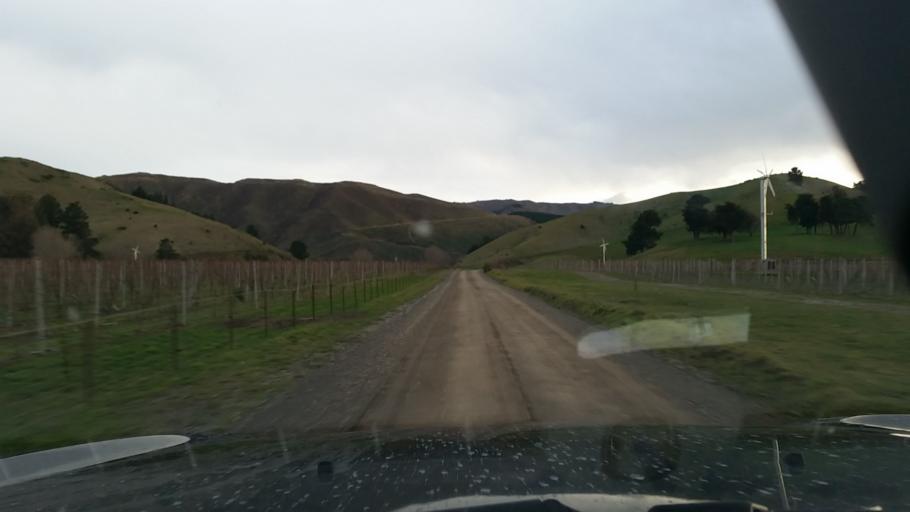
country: NZ
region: Nelson
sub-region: Nelson City
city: Nelson
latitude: -41.5829
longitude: 173.5097
